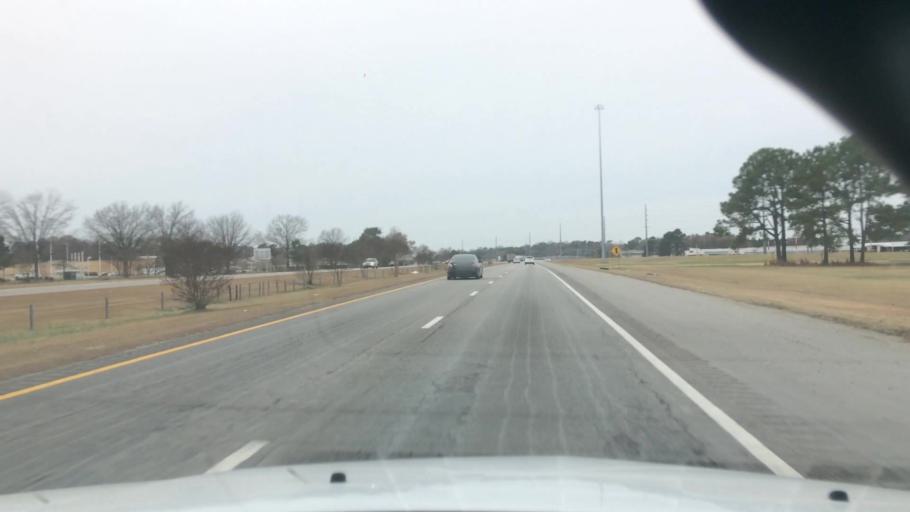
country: US
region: North Carolina
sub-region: Nash County
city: Rocky Mount
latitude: 35.9767
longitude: -77.8482
